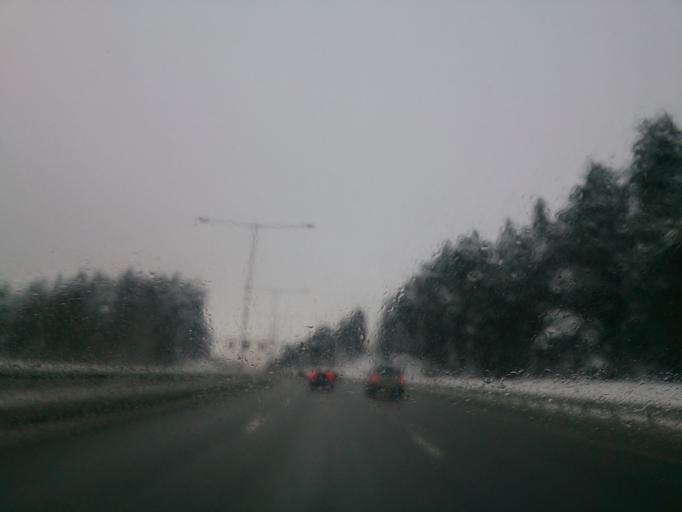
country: SE
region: Stockholm
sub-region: Botkyrka Kommun
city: Eriksberg
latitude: 59.2182
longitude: 17.7815
